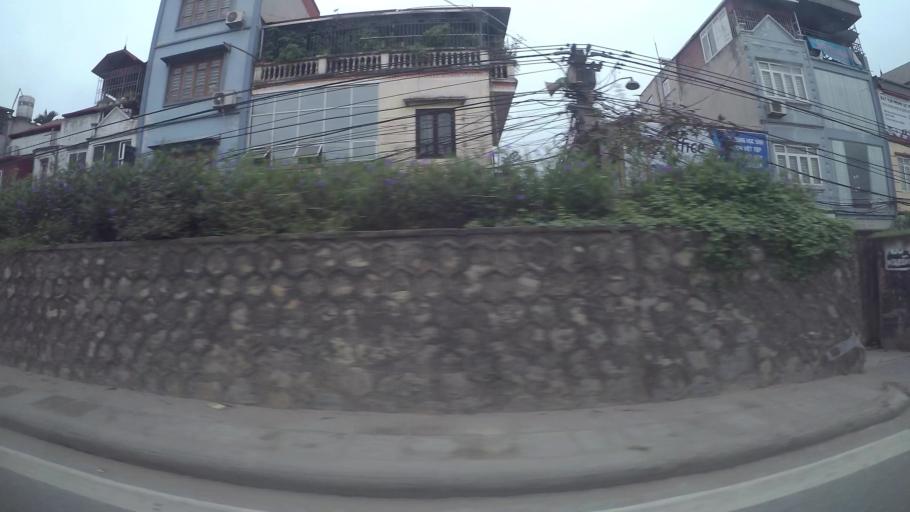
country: VN
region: Ha Noi
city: Hai BaTrung
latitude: 20.9998
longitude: 105.8860
